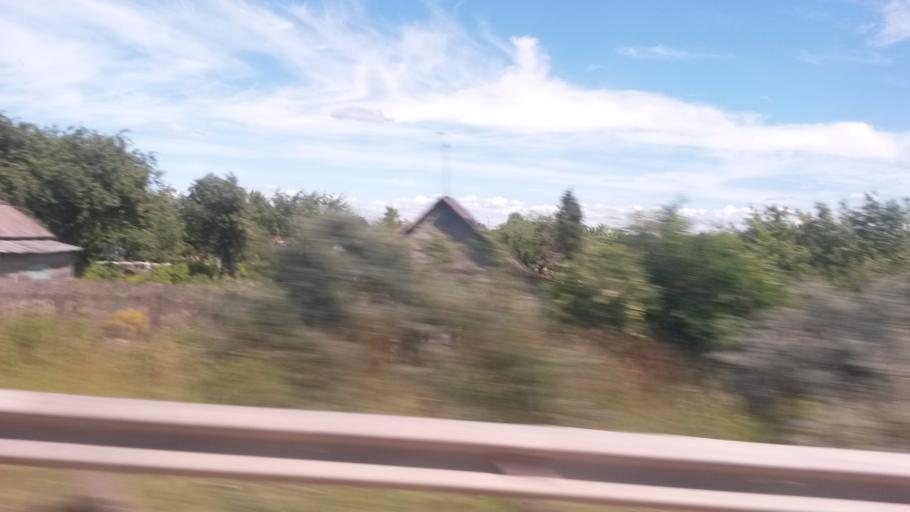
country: RU
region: Ivanovo
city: Staraya Vichuga
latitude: 57.2187
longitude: 41.8633
